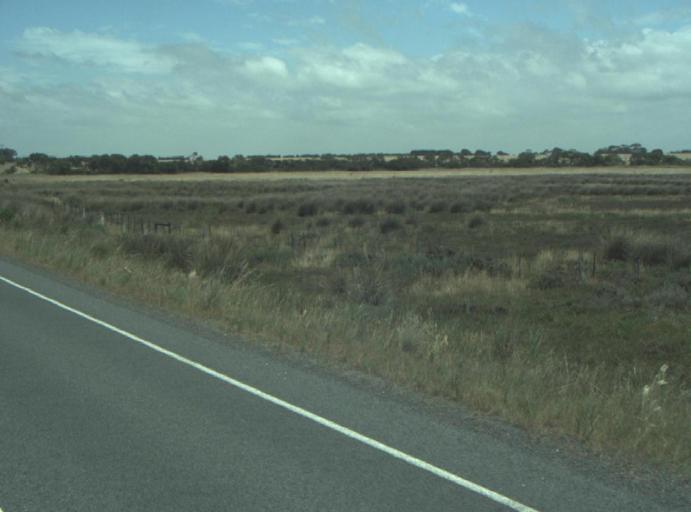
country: AU
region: Victoria
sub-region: Greater Geelong
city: Breakwater
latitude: -38.2920
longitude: 144.3755
